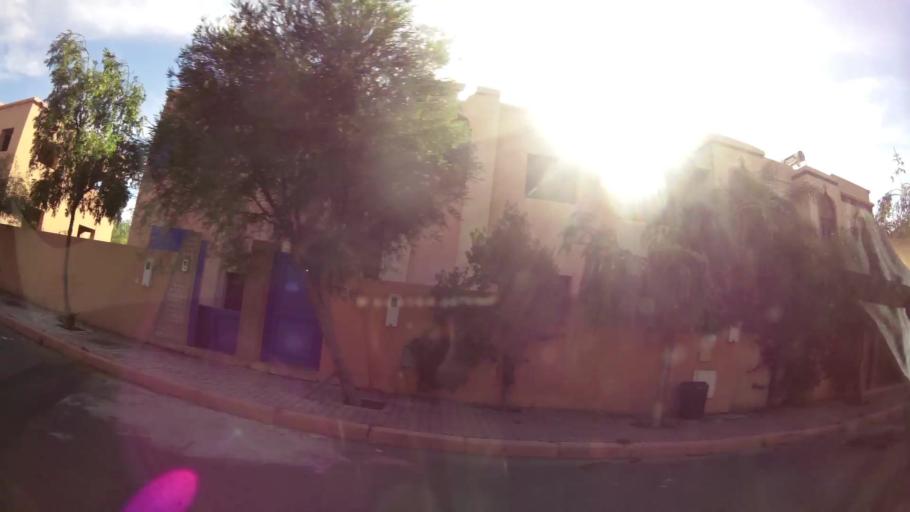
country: MA
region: Marrakech-Tensift-Al Haouz
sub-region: Marrakech
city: Marrakesh
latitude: 31.6765
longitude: -8.0547
